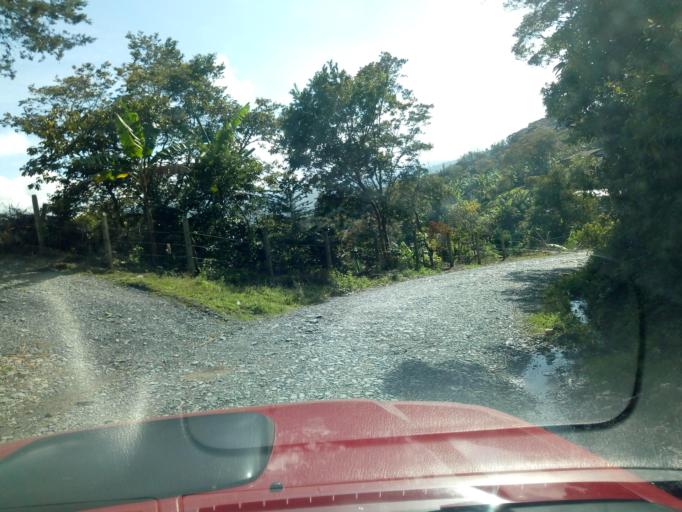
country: CO
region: Boyaca
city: Moniquira
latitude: 5.8849
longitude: -73.5441
